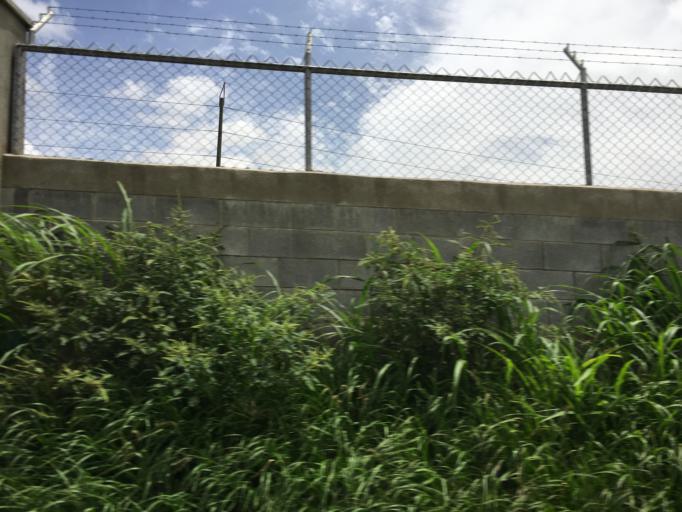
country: GT
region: Guatemala
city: Amatitlan
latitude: 14.4738
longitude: -90.6010
